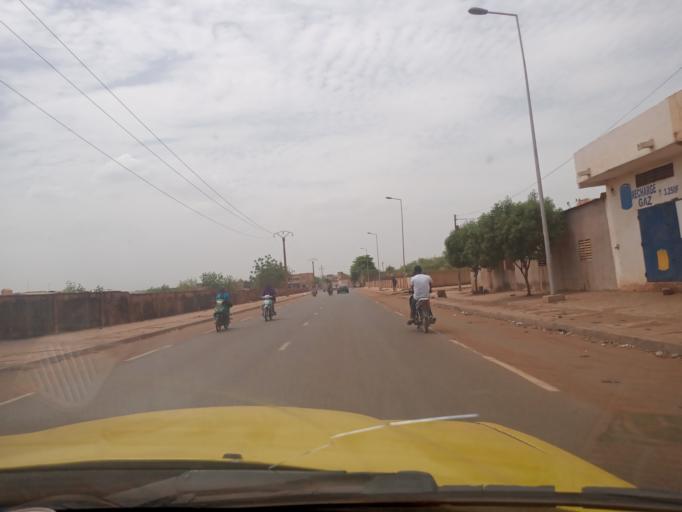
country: ML
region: Bamako
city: Bamako
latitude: 12.6022
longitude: -7.9610
